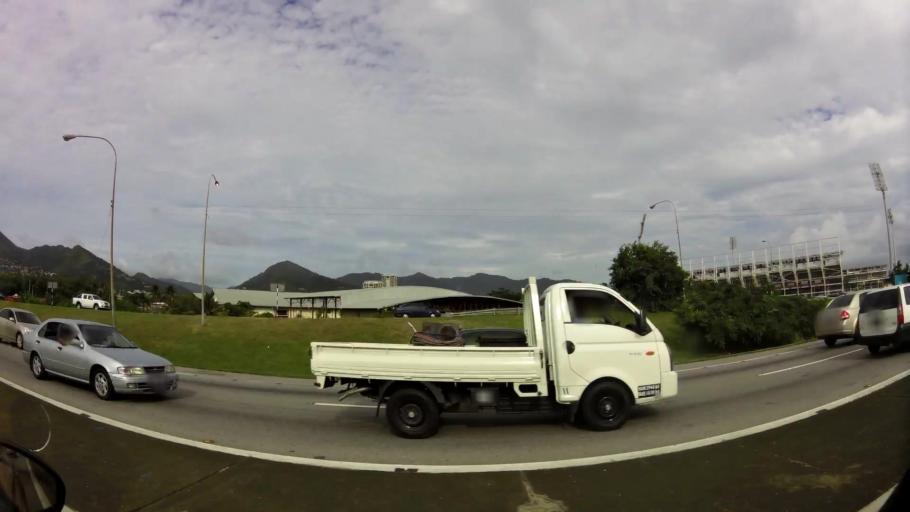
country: TT
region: City of Port of Spain
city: Mucurapo
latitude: 10.6623
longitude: -61.5358
